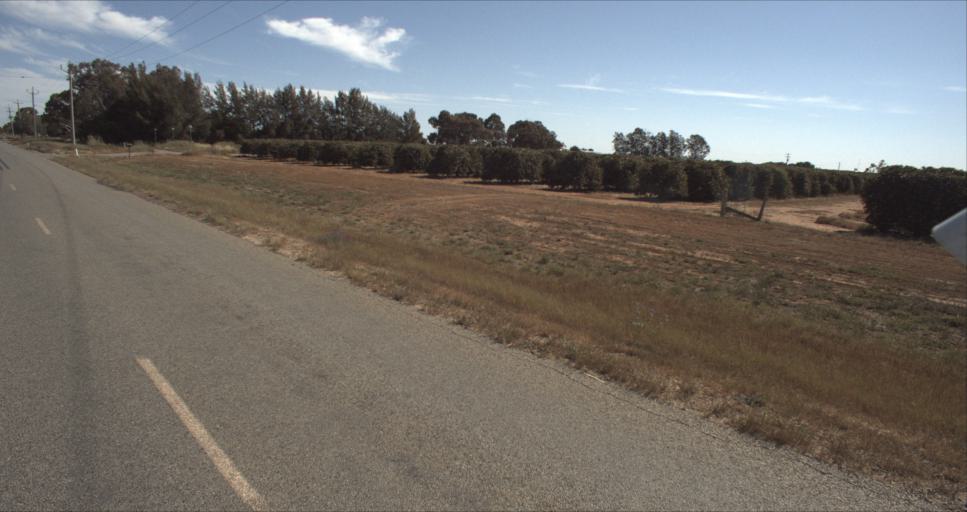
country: AU
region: New South Wales
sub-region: Leeton
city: Leeton
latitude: -34.5610
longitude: 146.3836
